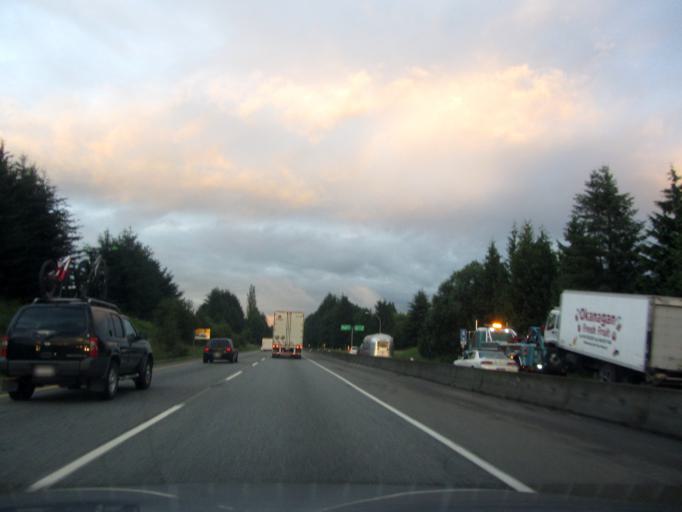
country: CA
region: British Columbia
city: Aldergrove
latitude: 49.1010
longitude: -122.4924
